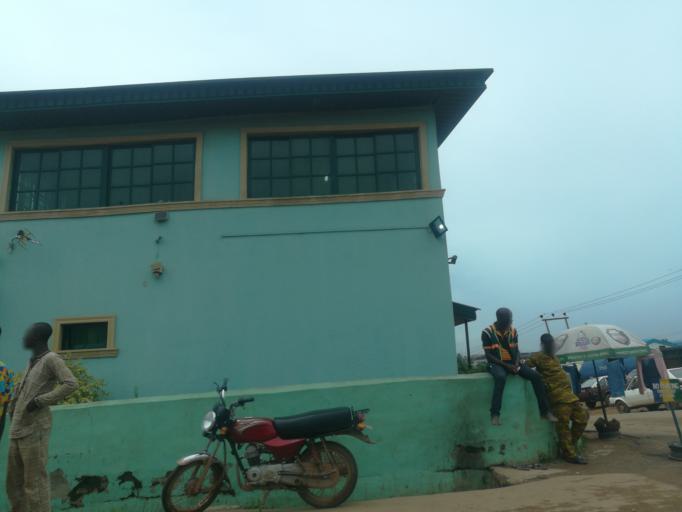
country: NG
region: Oyo
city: Ibadan
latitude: 7.3353
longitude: 3.8920
